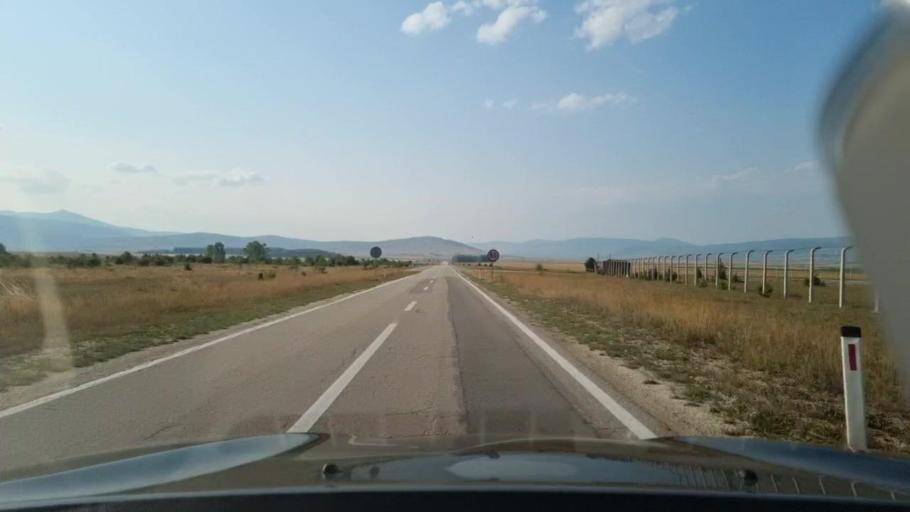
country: BA
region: Federation of Bosnia and Herzegovina
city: Glamoc
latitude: 44.0763
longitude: 16.8183
